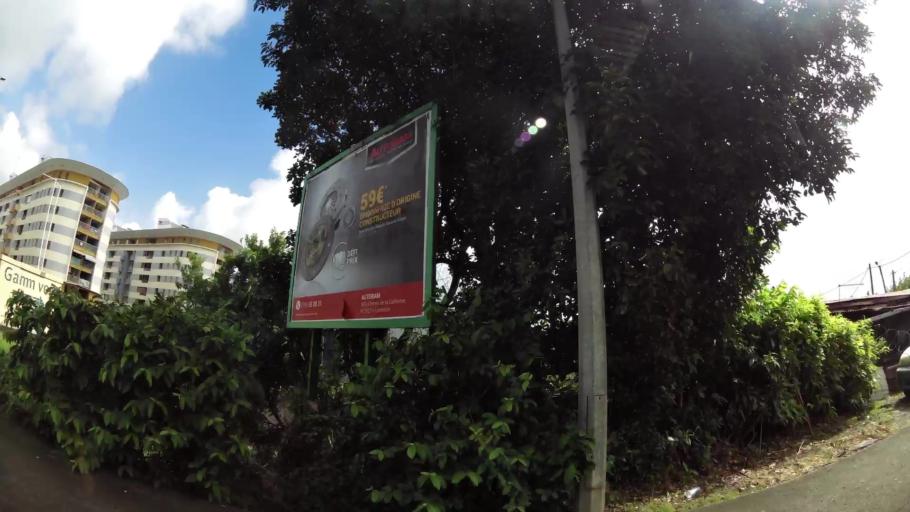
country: MQ
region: Martinique
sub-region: Martinique
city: Le Lamentin
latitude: 14.6124
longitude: -61.0005
